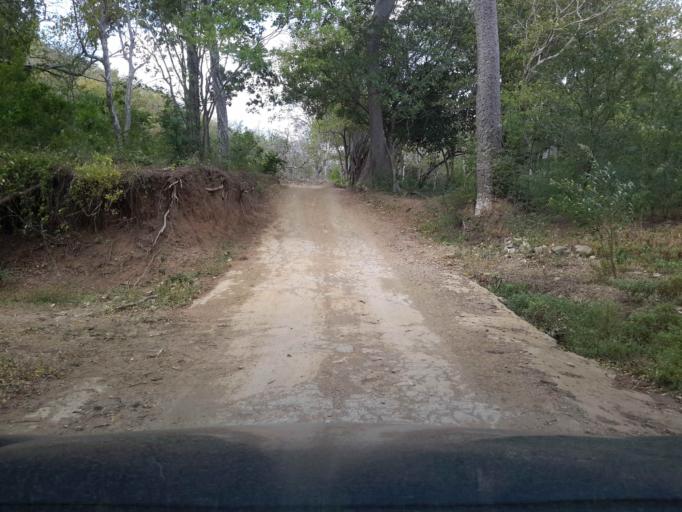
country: NI
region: Rivas
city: San Juan del Sur
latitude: 11.2150
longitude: -85.8390
